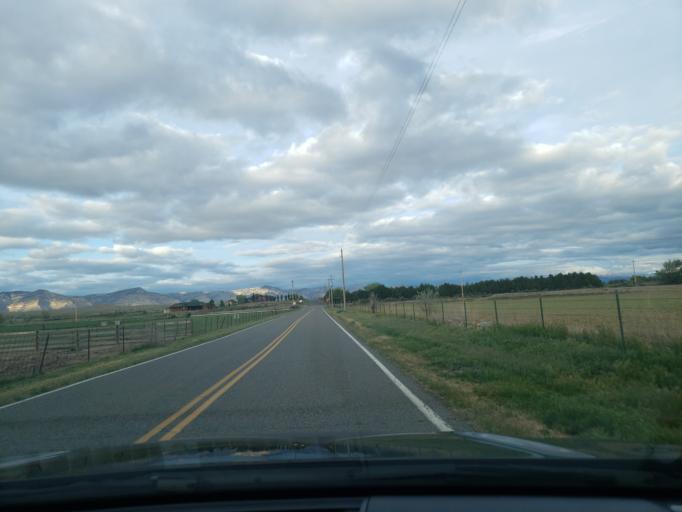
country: US
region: Colorado
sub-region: Mesa County
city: Fruita
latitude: 39.2221
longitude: -108.7037
